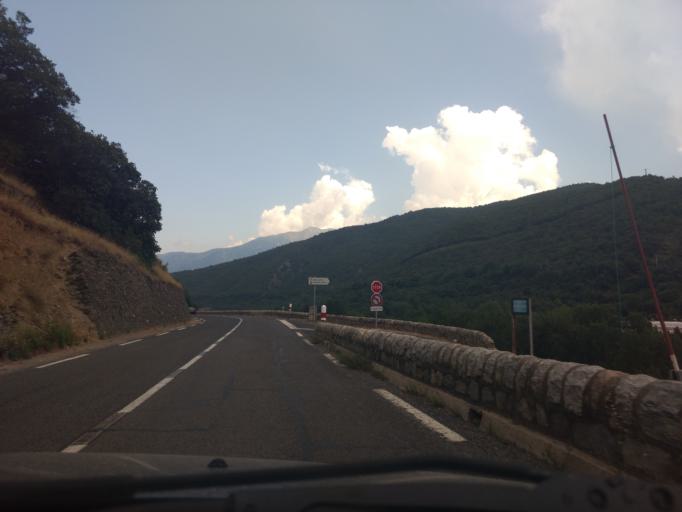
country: FR
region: Languedoc-Roussillon
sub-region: Departement des Pyrenees-Orientales
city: Vernet-les-Bains
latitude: 42.5617
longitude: 2.2927
